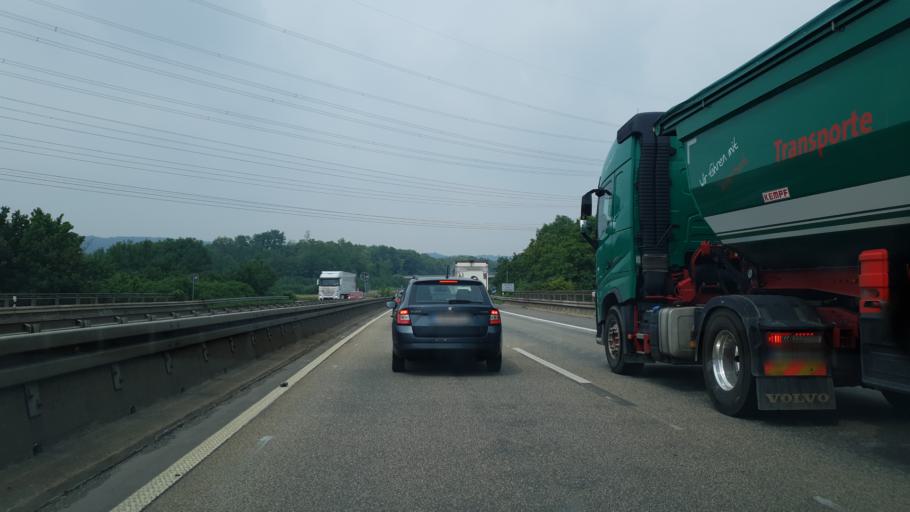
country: DE
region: North Rhine-Westphalia
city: Sprockhovel
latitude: 51.4113
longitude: 7.2608
